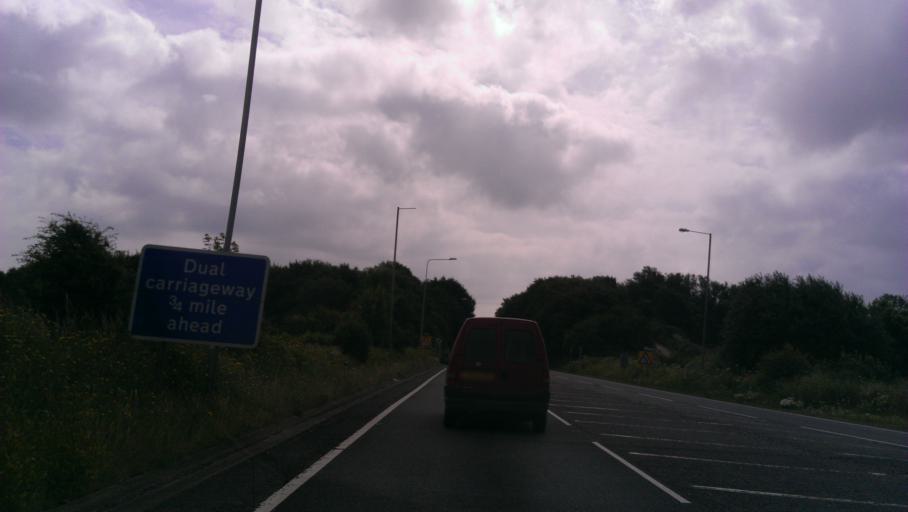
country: GB
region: England
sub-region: Kent
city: Dover
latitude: 51.1515
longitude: 1.3171
